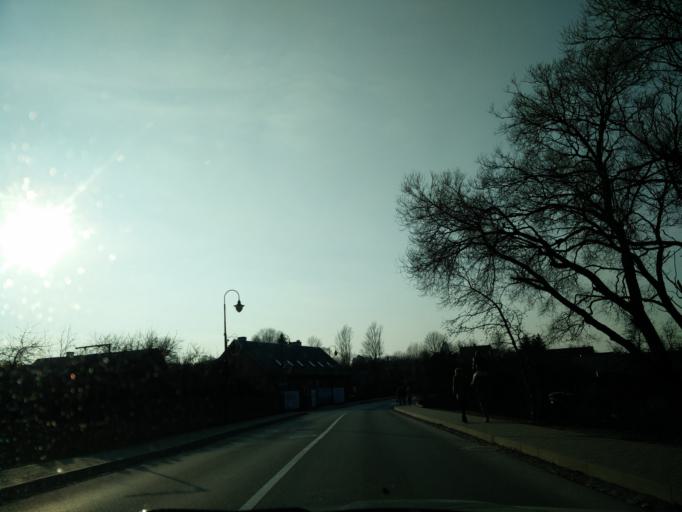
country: LT
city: Trakai
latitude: 54.6501
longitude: 24.9264
